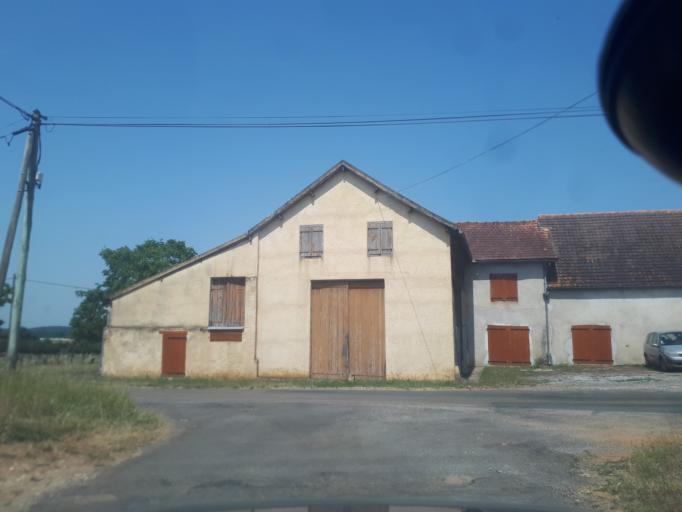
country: FR
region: Midi-Pyrenees
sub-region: Departement du Lot
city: Salviac
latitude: 44.7357
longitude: 1.3049
